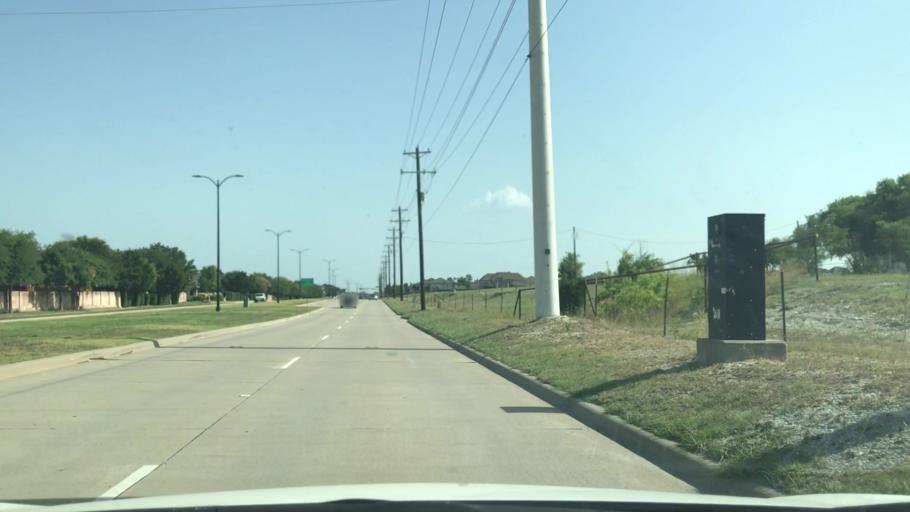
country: US
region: Texas
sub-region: Collin County
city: Frisco
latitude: 33.1355
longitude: -96.7507
